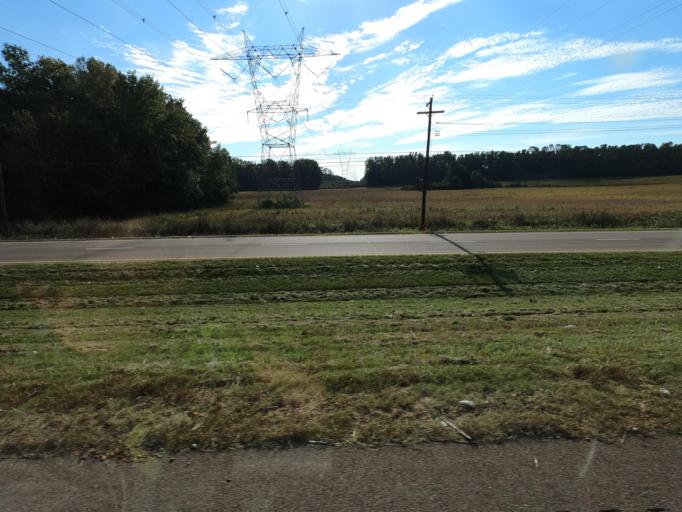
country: US
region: Tennessee
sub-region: Tipton County
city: Munford
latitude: 35.4102
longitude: -89.8335
